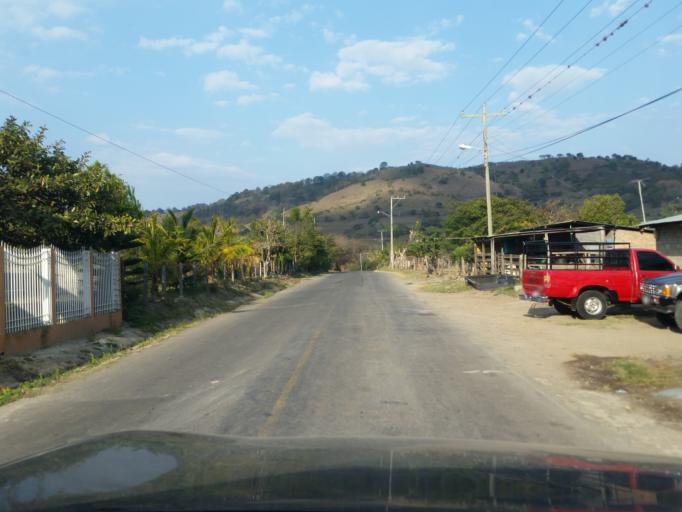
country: NI
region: Jinotega
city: San Rafael del Norte
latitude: 13.1975
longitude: -86.1160
